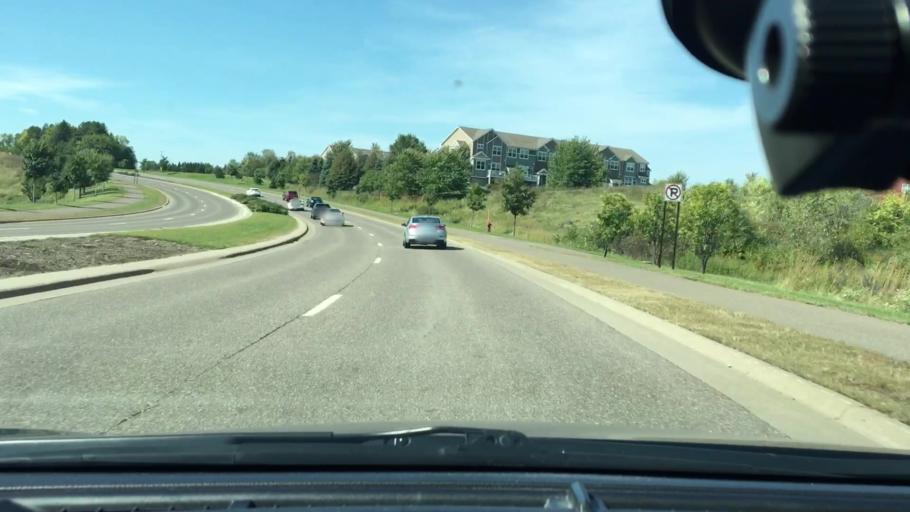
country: US
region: Minnesota
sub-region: Hennepin County
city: Maple Grove
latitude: 45.0846
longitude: -93.4930
